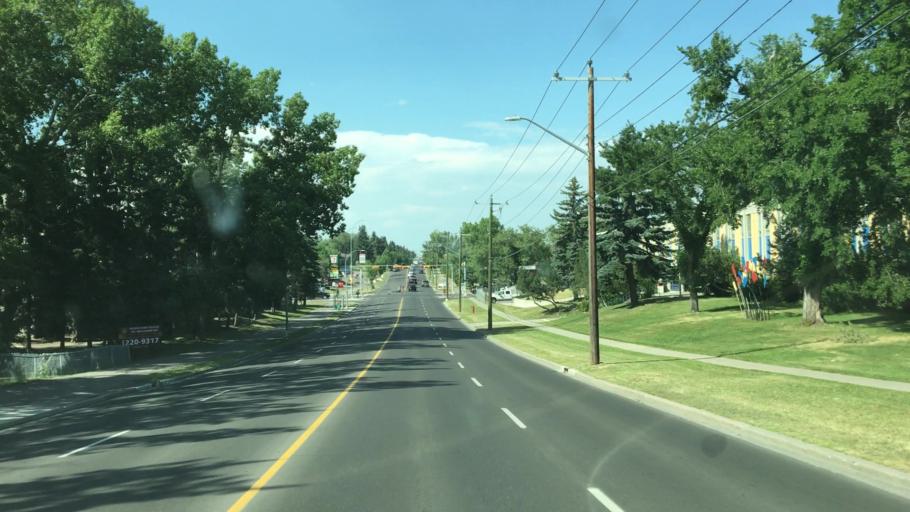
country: CA
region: Alberta
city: Calgary
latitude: 51.0858
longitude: -114.0716
